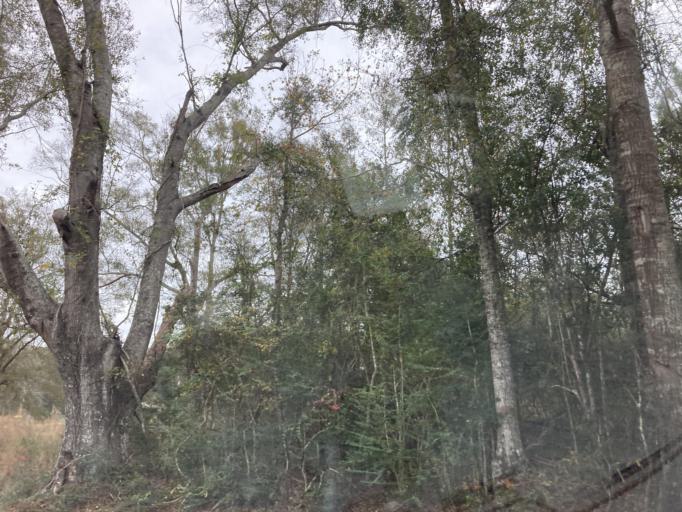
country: US
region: Mississippi
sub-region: Forrest County
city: Hattiesburg
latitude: 31.1635
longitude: -89.2189
